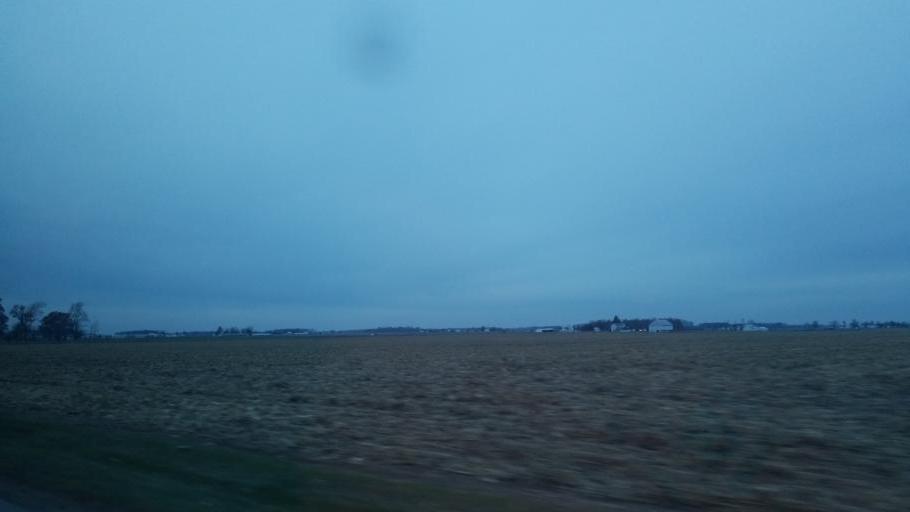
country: US
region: Indiana
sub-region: Adams County
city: Berne
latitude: 40.7309
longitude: -84.9514
